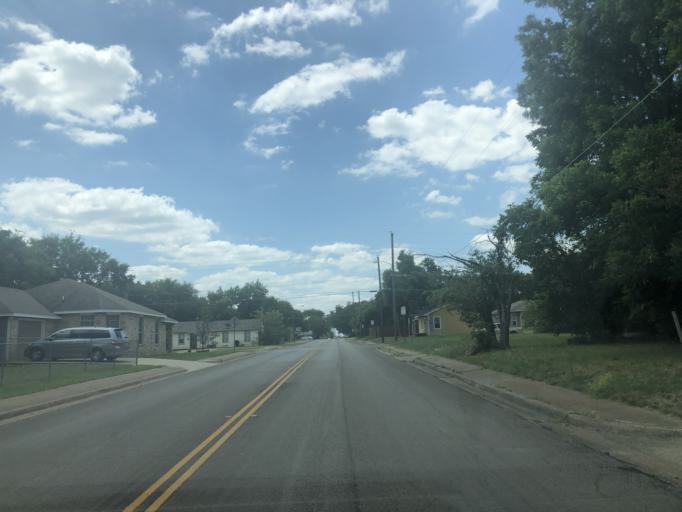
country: US
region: Texas
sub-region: Dallas County
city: Grand Prairie
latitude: 32.7366
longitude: -97.0327
